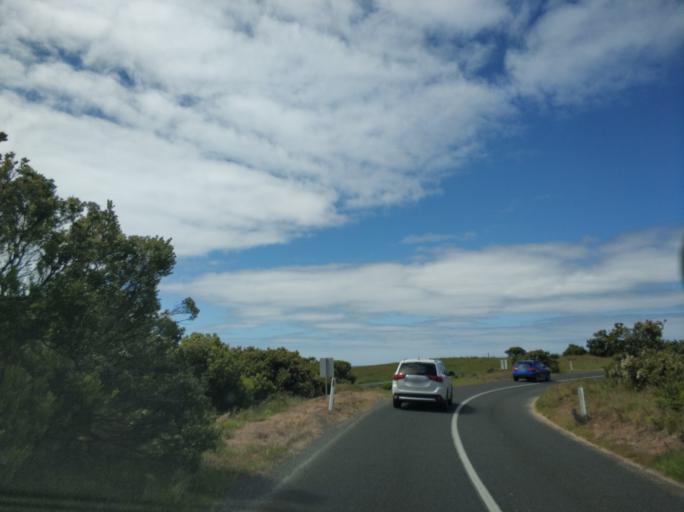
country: AU
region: Victoria
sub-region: Colac-Otway
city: Apollo Bay
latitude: -38.8484
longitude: 143.5364
